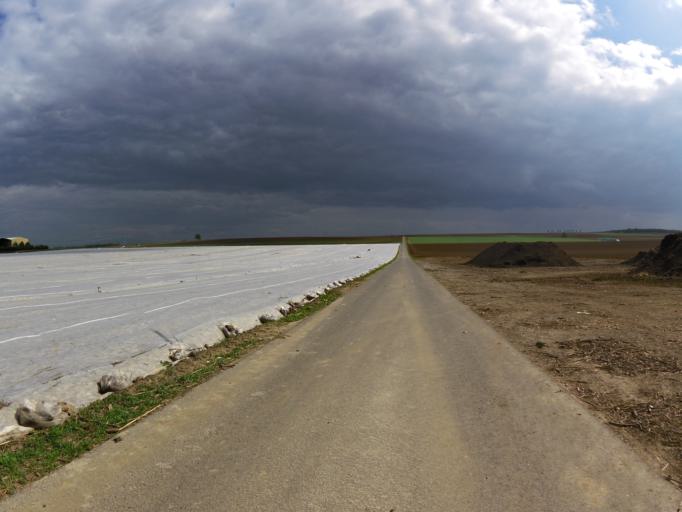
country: DE
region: Bavaria
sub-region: Regierungsbezirk Unterfranken
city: Oberpleichfeld
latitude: 49.8665
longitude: 10.0808
